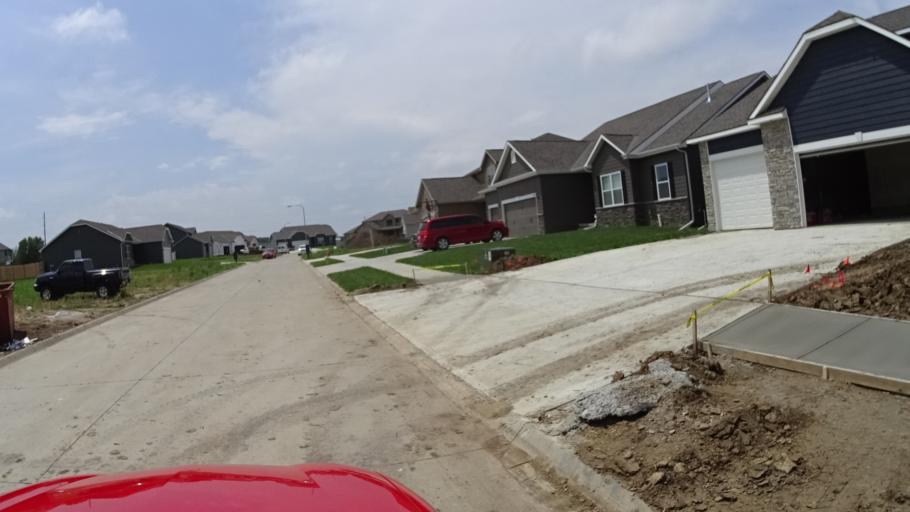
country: US
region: Nebraska
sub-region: Sarpy County
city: Papillion
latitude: 41.1462
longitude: -95.9835
